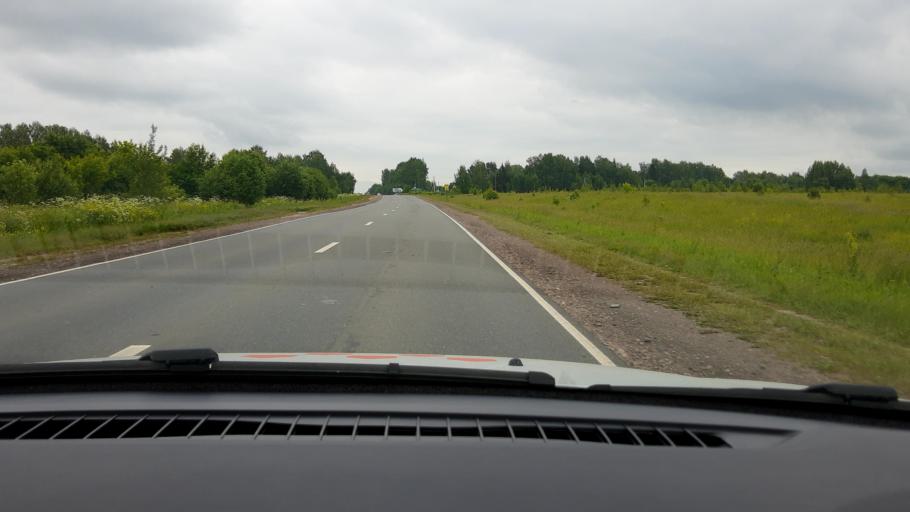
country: RU
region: Nizjnij Novgorod
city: Bogorodsk
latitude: 56.0870
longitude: 43.5226
